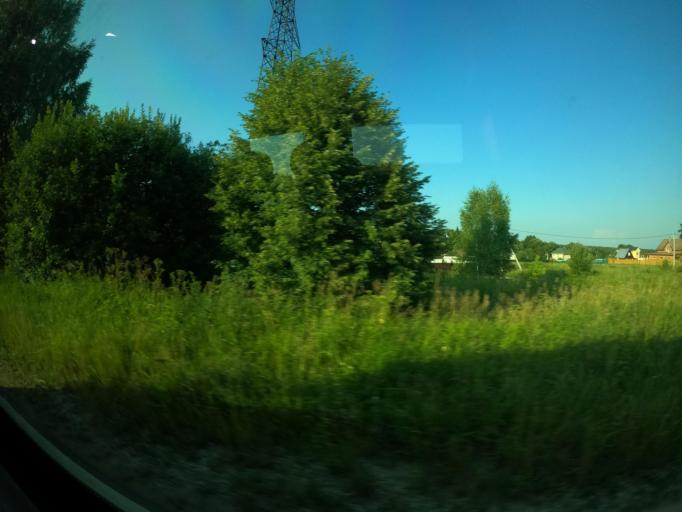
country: RU
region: Moskovskaya
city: Protvino
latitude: 54.9177
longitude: 37.2695
